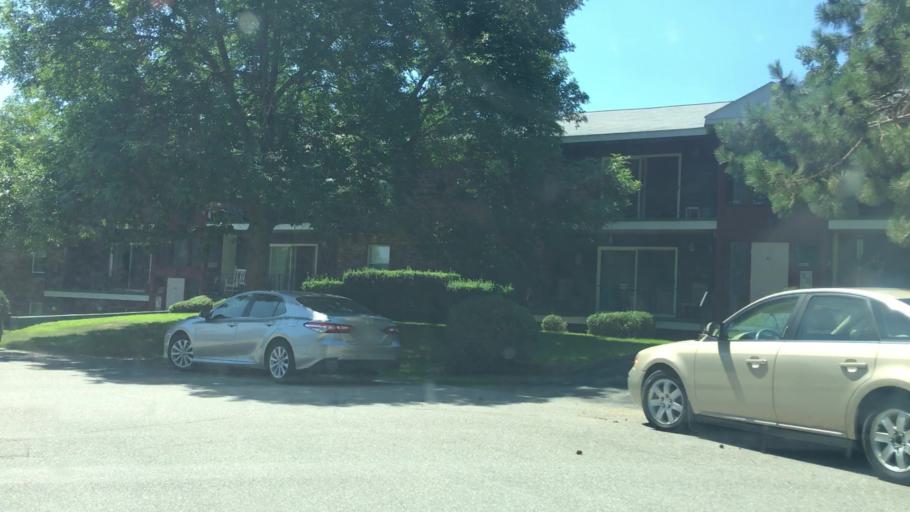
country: US
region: Maine
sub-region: Penobscot County
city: Bangor
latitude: 44.8091
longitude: -68.7974
